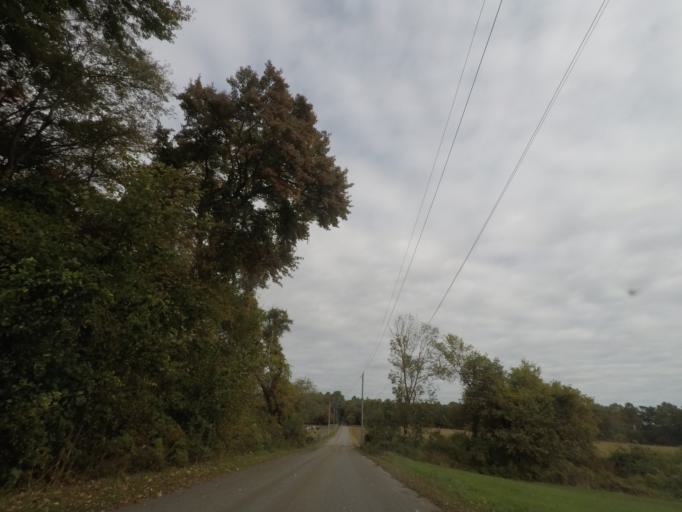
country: US
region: Connecticut
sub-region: Windham County
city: Thompson
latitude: 41.9592
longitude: -71.8336
